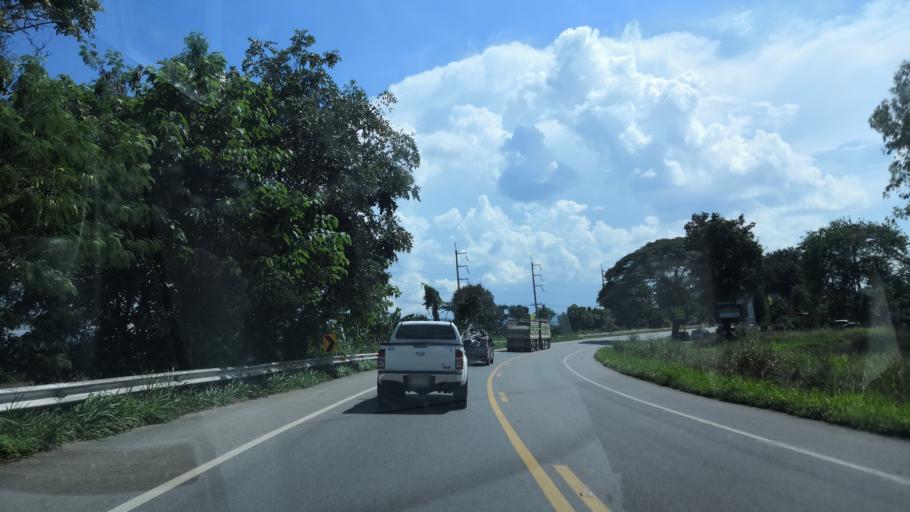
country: TH
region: Chiang Rai
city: Mae Suai
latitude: 19.6254
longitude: 99.5189
